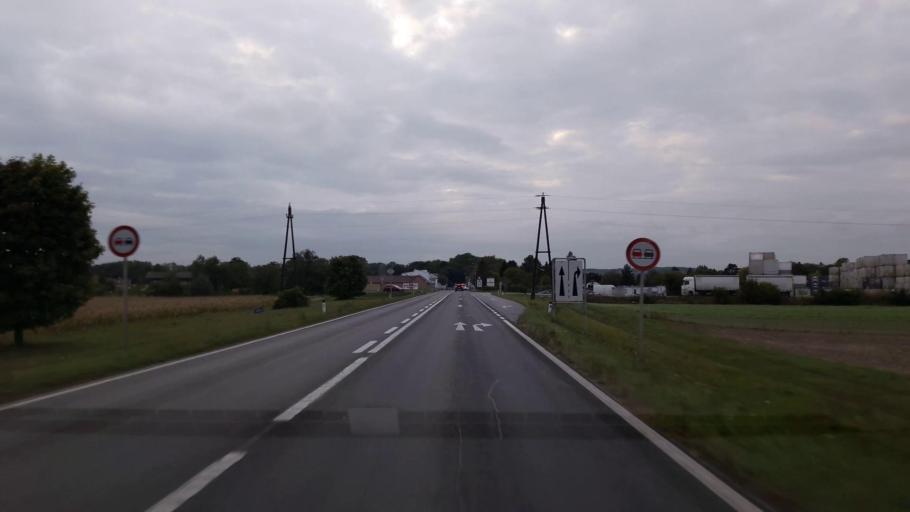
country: AT
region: Lower Austria
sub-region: Politischer Bezirk Wien-Umgebung
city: Schwadorf
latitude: 48.0683
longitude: 16.5934
